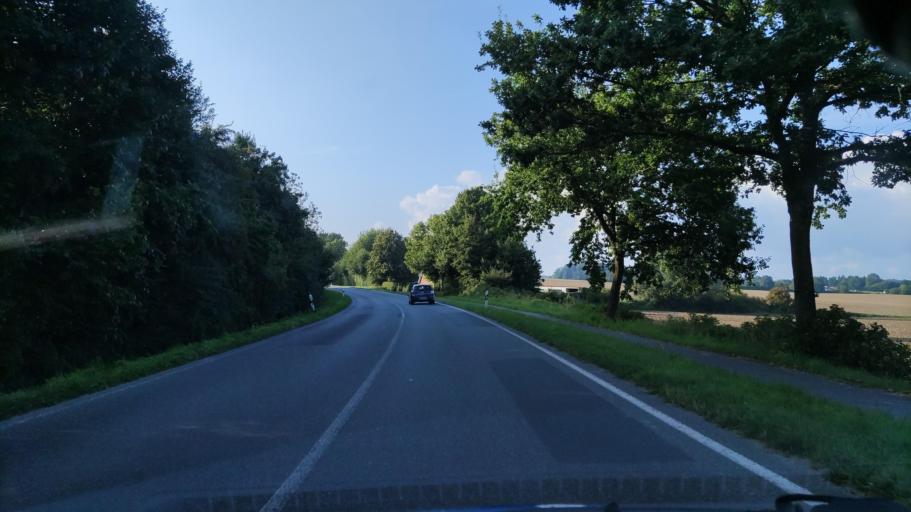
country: DE
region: Schleswig-Holstein
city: Ahrensbok
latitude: 53.9681
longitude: 10.6006
